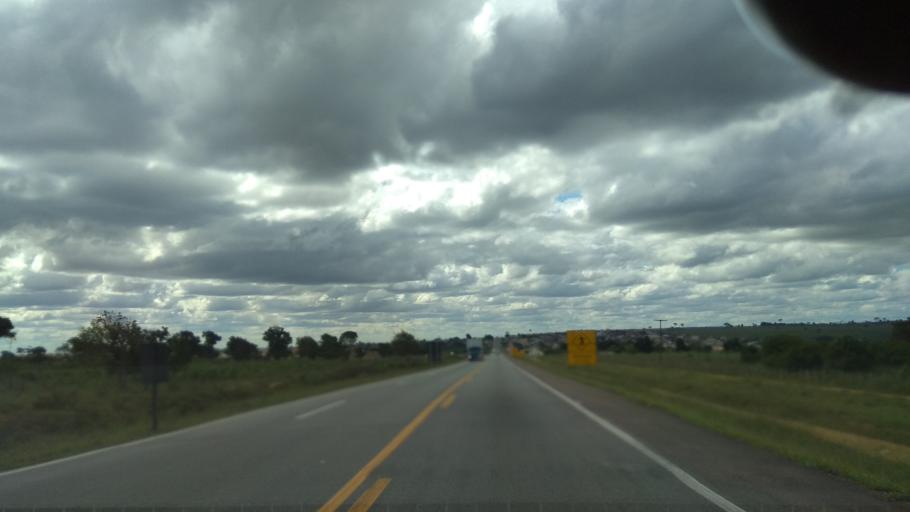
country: BR
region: Bahia
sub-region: Santa Ines
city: Santa Ines
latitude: -13.0878
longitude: -39.9626
